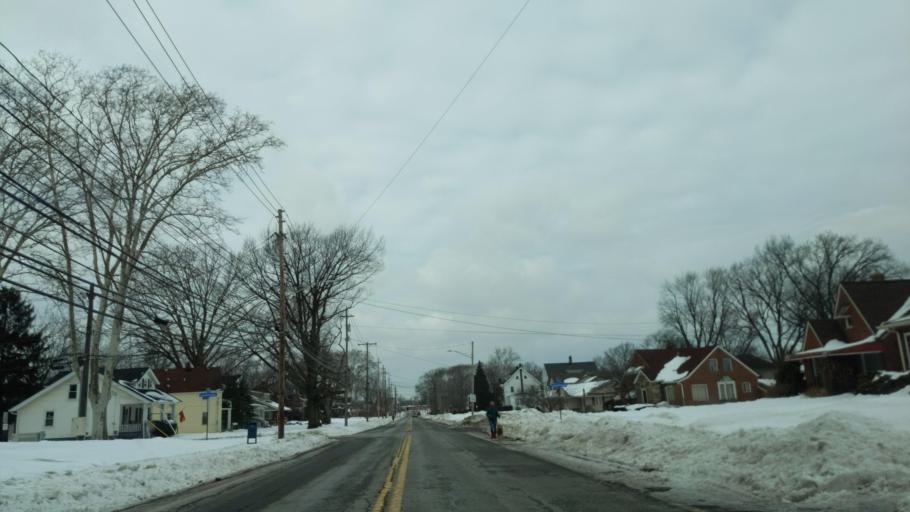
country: US
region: Ohio
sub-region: Cuyahoga County
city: Brooklyn Heights
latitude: 41.4273
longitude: -81.6919
